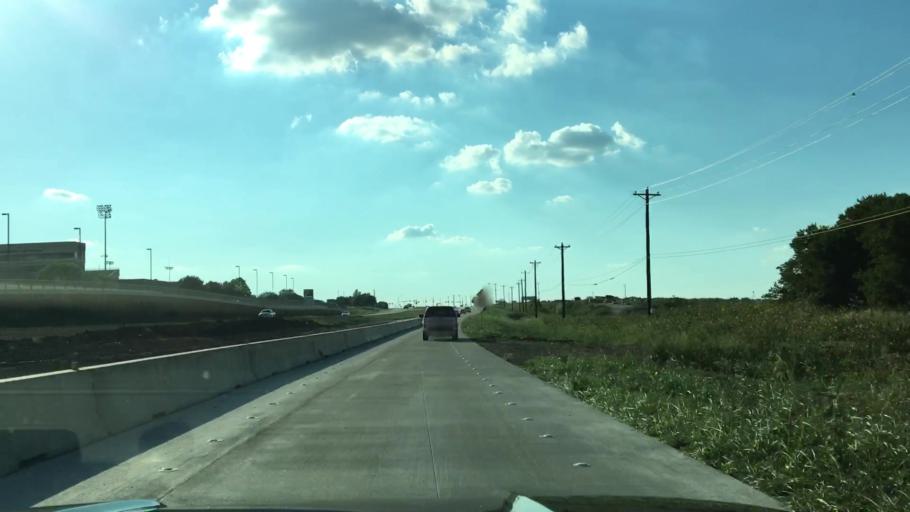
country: US
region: Texas
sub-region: Denton County
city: Justin
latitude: 33.0320
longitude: -97.3164
